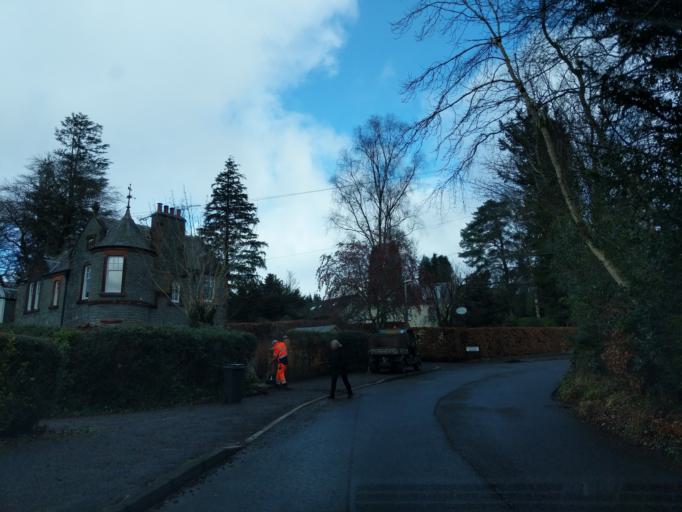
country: GB
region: Scotland
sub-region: Dumfries and Galloway
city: Moffat
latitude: 55.3345
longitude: -3.4370
